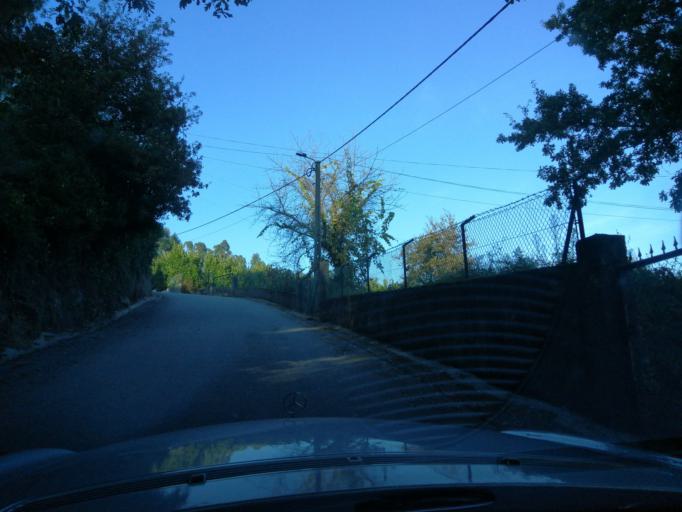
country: PT
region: Braga
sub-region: Braga
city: Oliveira
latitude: 41.4621
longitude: -8.4513
